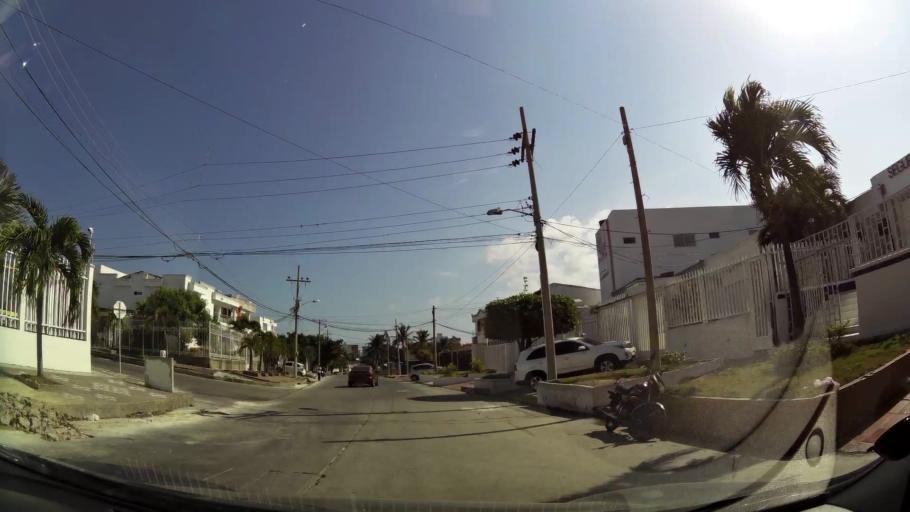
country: CO
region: Atlantico
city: Barranquilla
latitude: 10.9871
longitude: -74.8235
